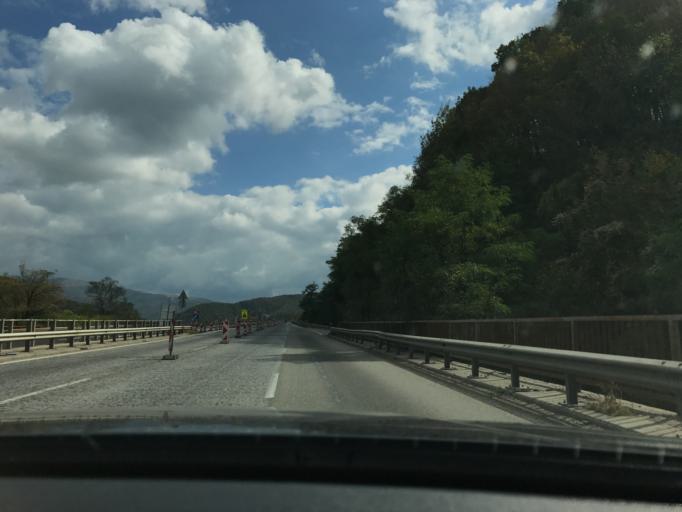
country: BG
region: Sofiya
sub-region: Obshtina Botevgrad
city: Botevgrad
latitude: 42.8104
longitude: 23.8014
